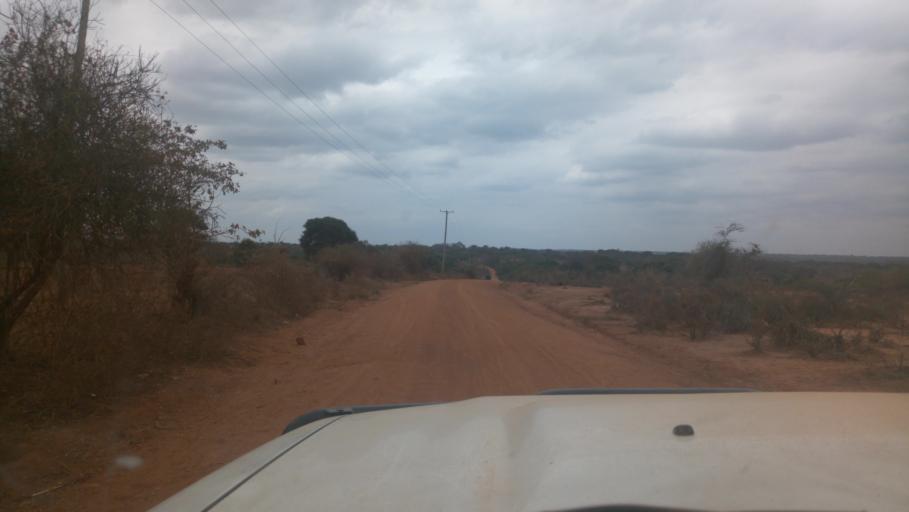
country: KE
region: Kitui
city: Kitui
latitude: -1.6242
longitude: 37.8758
